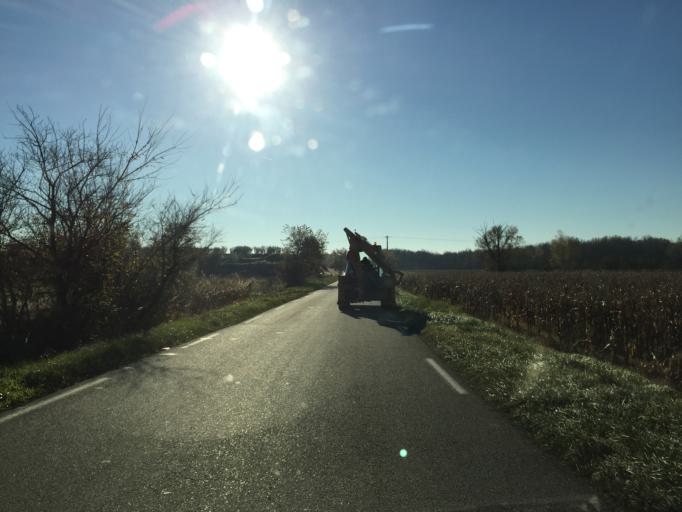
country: FR
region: Provence-Alpes-Cote d'Azur
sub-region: Departement du Vaucluse
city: Bedarrides
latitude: 44.0308
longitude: 4.9142
